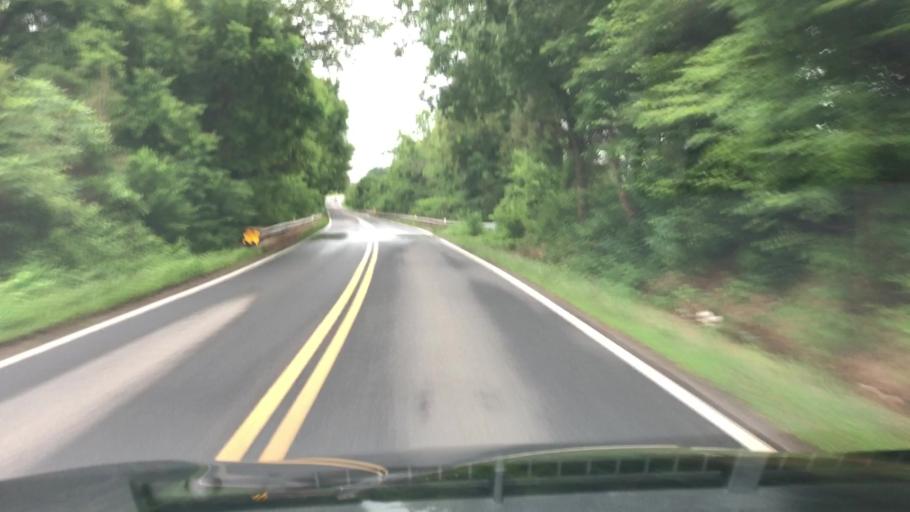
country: US
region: Virginia
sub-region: Prince William County
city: Nokesville
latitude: 38.6077
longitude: -77.6059
